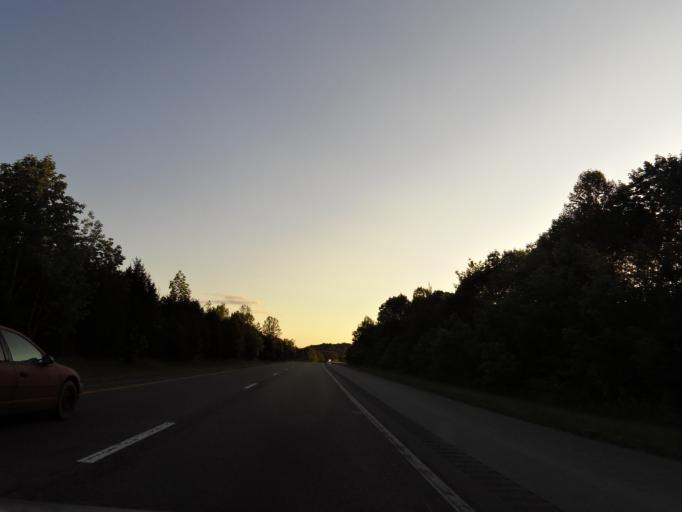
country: US
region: Tennessee
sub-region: Washington County
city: Fall Branch
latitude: 36.3630
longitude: -82.6895
